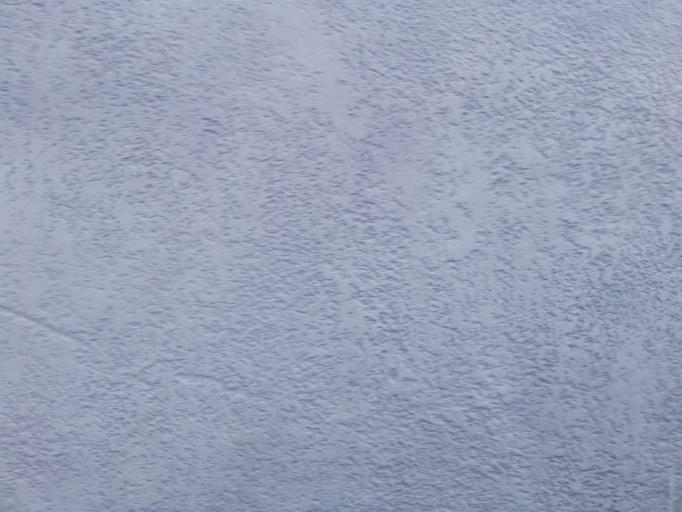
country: MU
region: Port Louis
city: Port Louis
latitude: -20.1618
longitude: 57.4822
